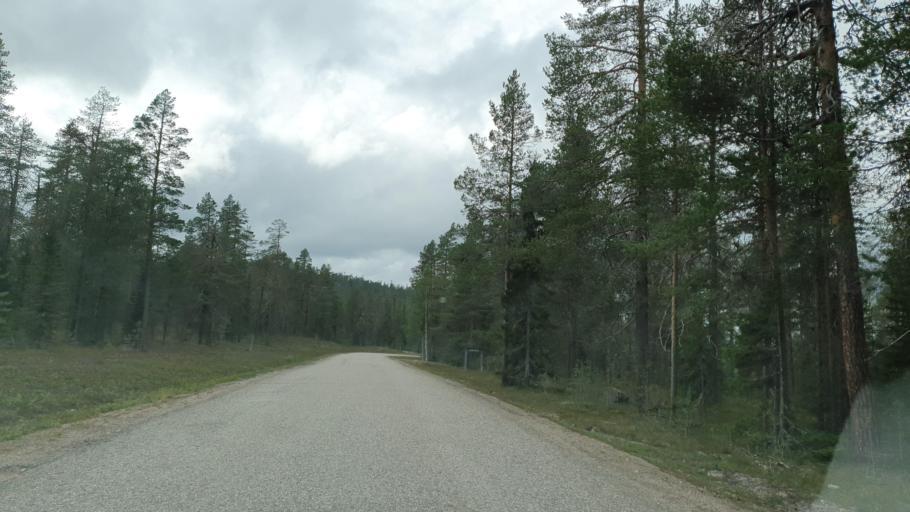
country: FI
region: Lapland
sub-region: Tunturi-Lappi
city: Kolari
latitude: 67.5224
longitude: 24.1731
